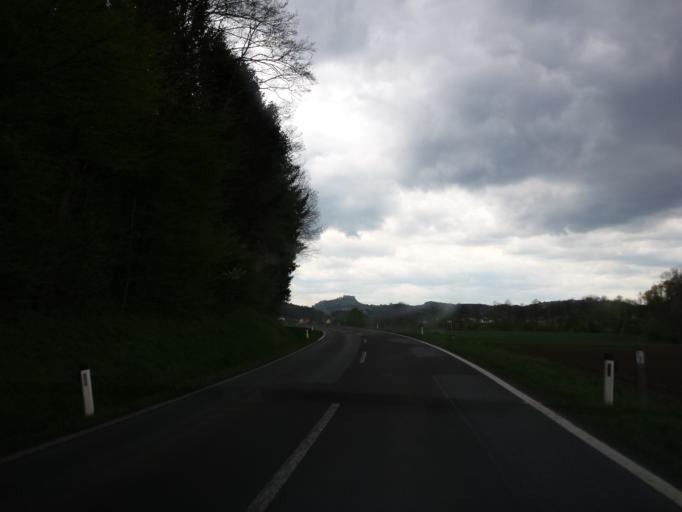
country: AT
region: Styria
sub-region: Politischer Bezirk Suedoststeiermark
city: Hatzendorf
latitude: 46.9850
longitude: 15.9933
